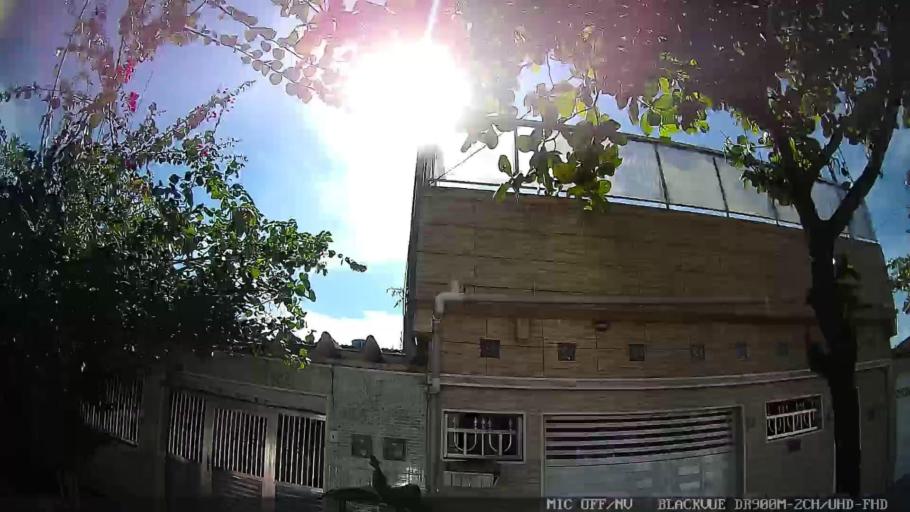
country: BR
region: Sao Paulo
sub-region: Guaruja
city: Guaruja
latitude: -23.9440
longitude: -46.2810
